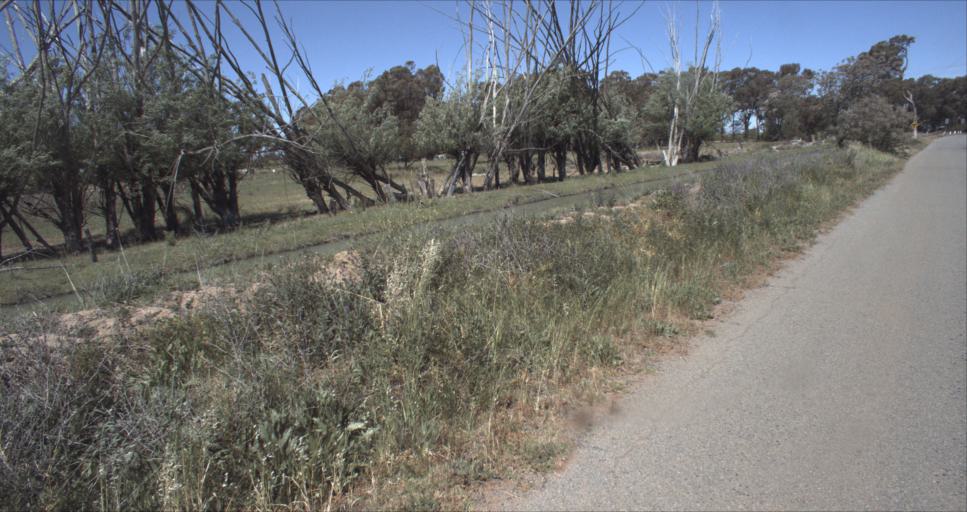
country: AU
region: New South Wales
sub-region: Leeton
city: Leeton
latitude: -34.5435
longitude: 146.3533
